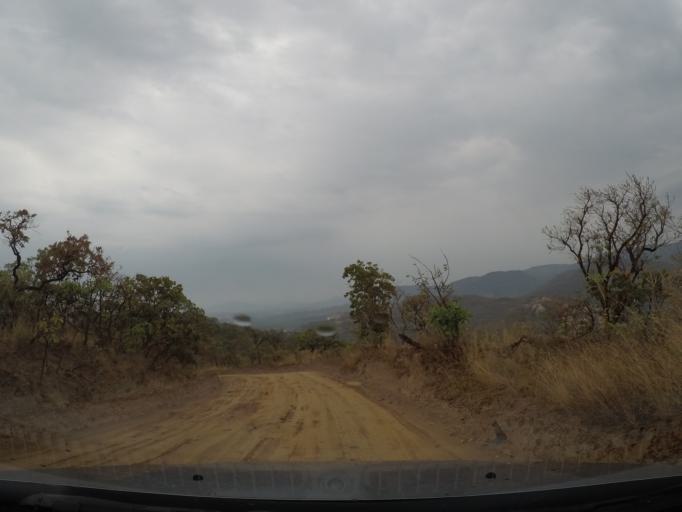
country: BR
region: Goias
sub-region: Pirenopolis
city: Pirenopolis
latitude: -15.8390
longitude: -48.9148
